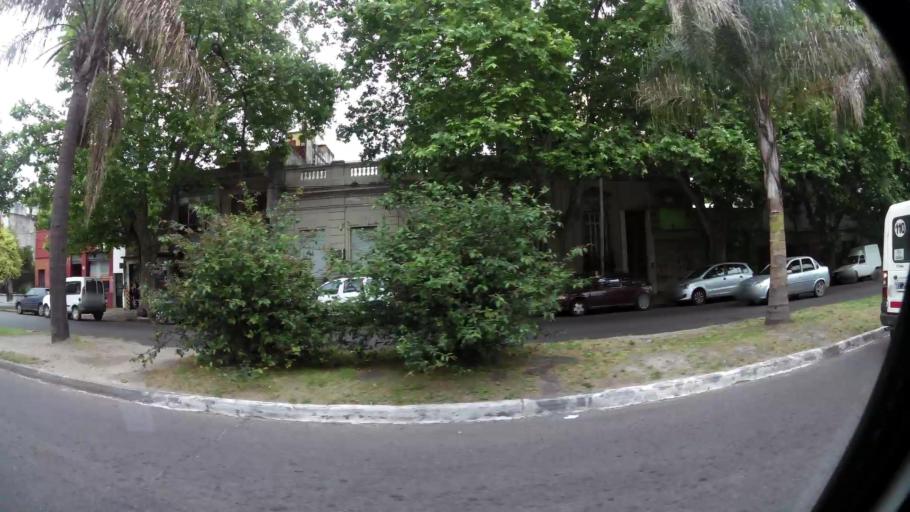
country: AR
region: Buenos Aires
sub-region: Partido de La Plata
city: La Plata
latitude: -34.9293
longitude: -57.9540
